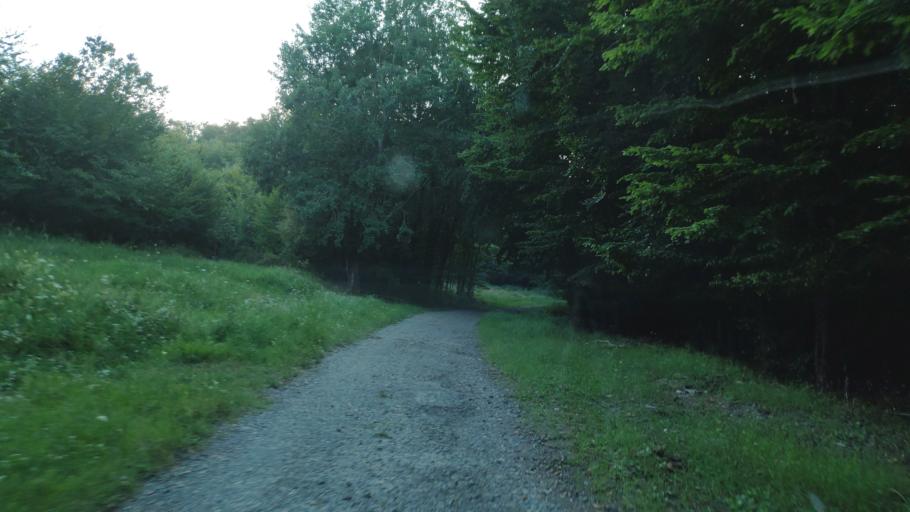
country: SK
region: Kosicky
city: Secovce
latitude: 48.5889
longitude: 21.5267
